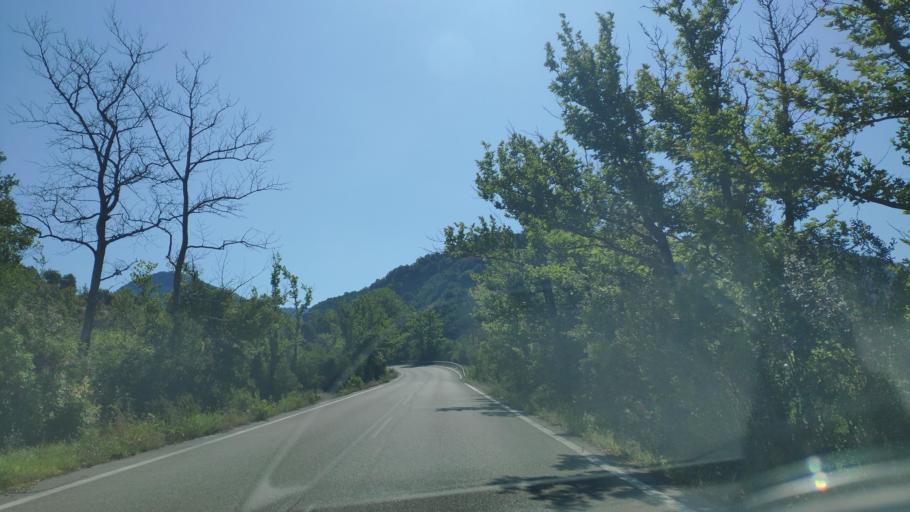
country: GR
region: West Greece
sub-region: Nomos Aitolias kai Akarnanias
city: Sardinia
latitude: 38.9236
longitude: 21.3755
